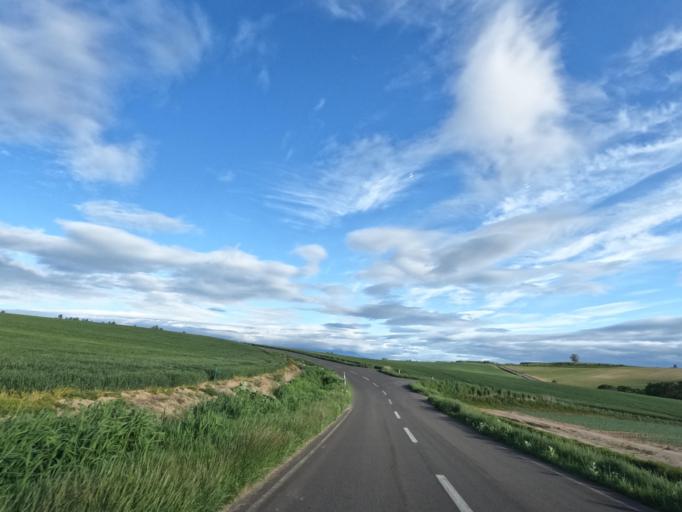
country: JP
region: Hokkaido
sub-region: Asahikawa-shi
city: Asahikawa
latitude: 43.6248
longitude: 142.4382
